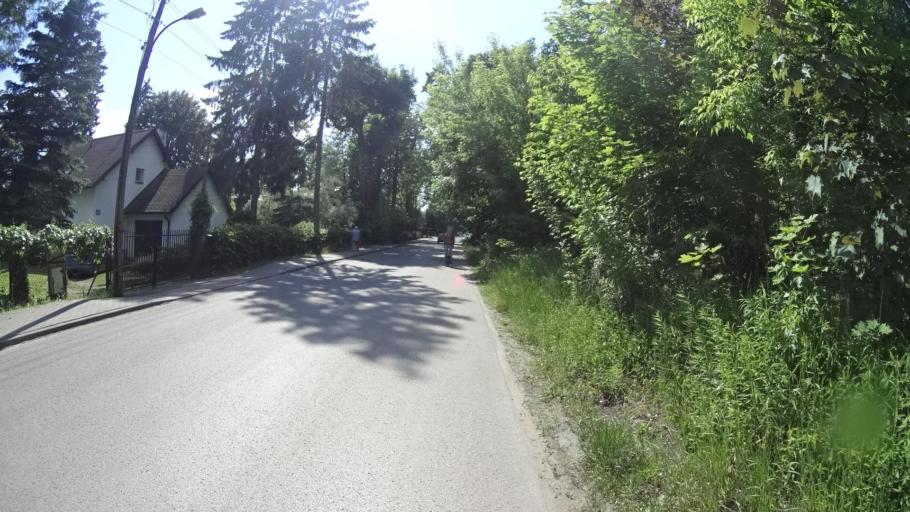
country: PL
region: Masovian Voivodeship
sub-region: Powiat piaseczynski
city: Mysiadlo
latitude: 52.1155
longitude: 21.0272
